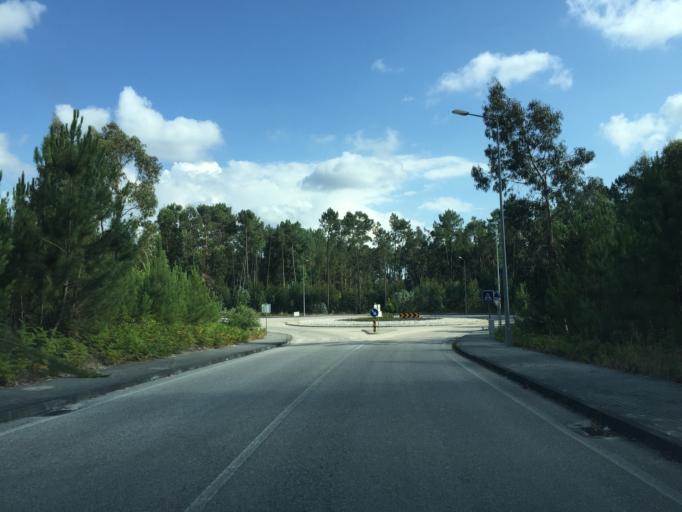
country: PT
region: Leiria
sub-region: Leiria
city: Monte Redondo
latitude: 39.9436
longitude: -8.7983
